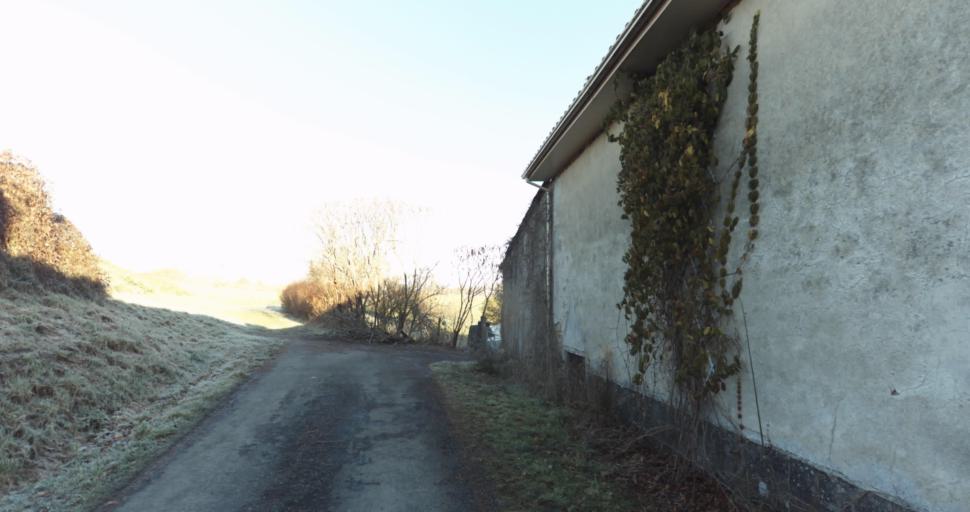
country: FR
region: Limousin
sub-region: Departement de la Haute-Vienne
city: Aixe-sur-Vienne
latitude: 45.8047
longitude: 1.1466
